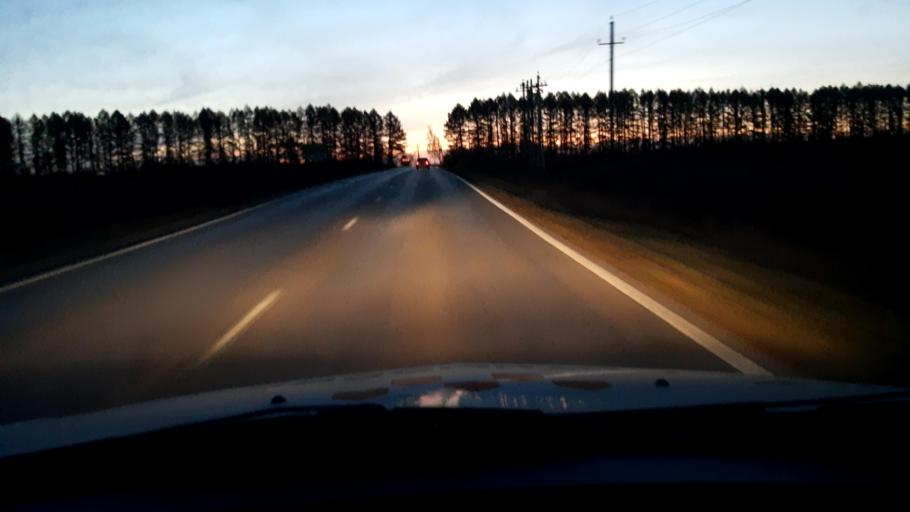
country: RU
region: Bashkortostan
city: Iglino
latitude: 54.7390
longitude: 56.2512
